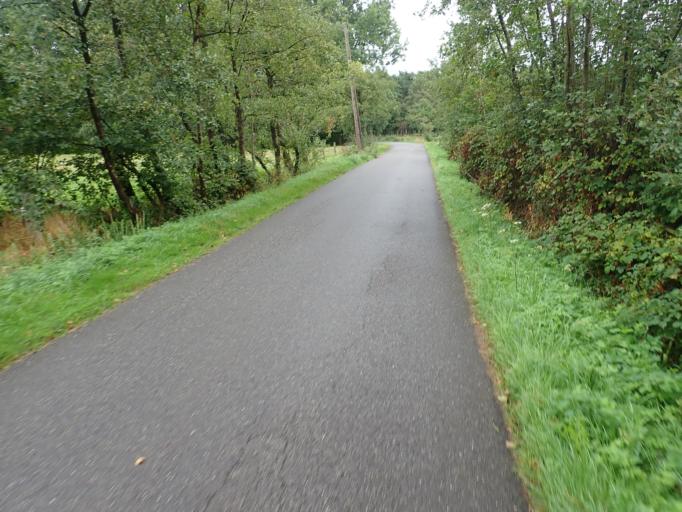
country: BE
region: Flanders
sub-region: Provincie Antwerpen
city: Zoersel
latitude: 51.2514
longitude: 4.7320
